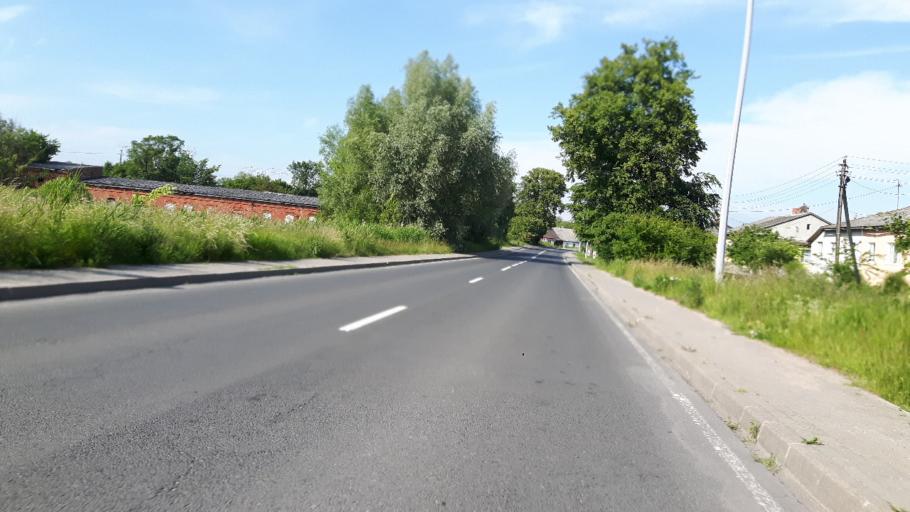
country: RU
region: Kaliningrad
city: Mamonovo
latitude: 54.4589
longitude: 19.9278
